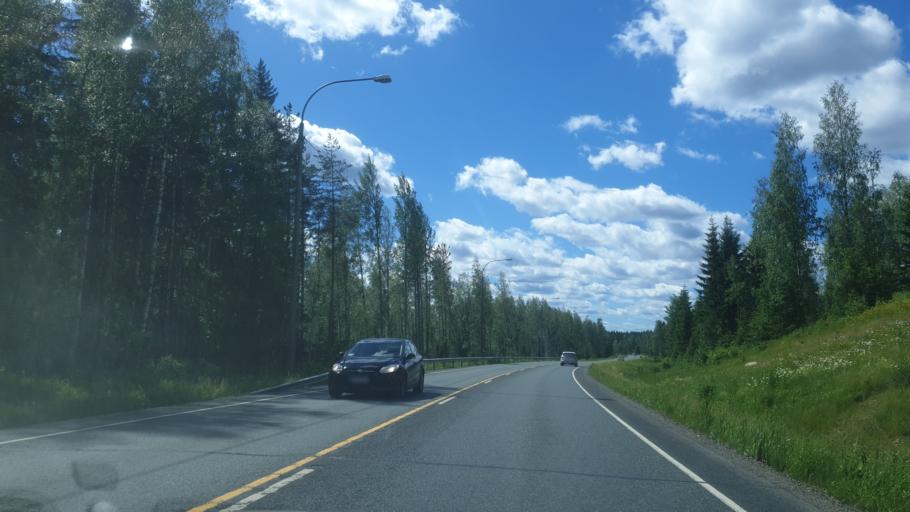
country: FI
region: Northern Savo
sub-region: Varkaus
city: Leppaevirta
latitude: 62.6049
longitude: 27.6203
